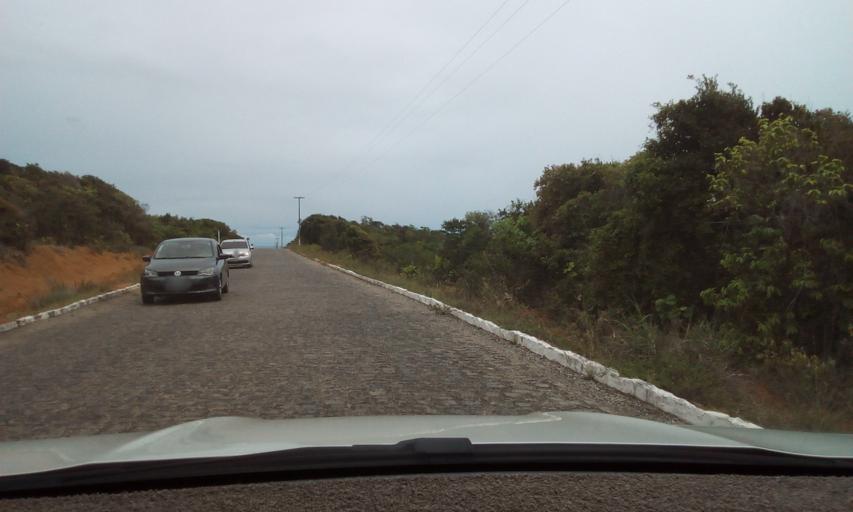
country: BR
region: Paraiba
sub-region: Conde
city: Conde
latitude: -7.3341
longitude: -34.8029
